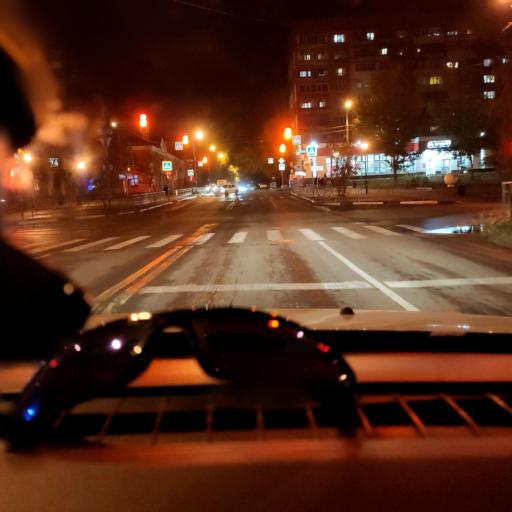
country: RU
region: Samara
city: Samara
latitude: 53.2284
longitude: 50.2549
